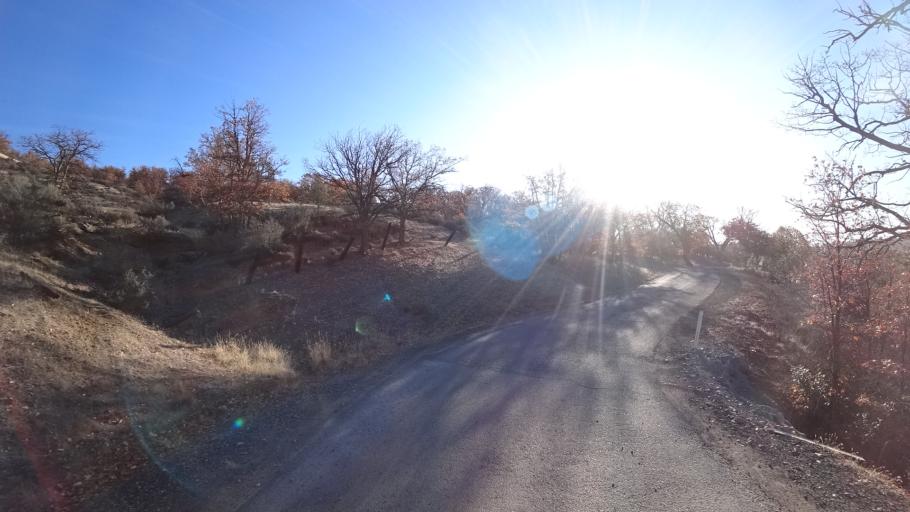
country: US
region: Oregon
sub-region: Jackson County
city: Ashland
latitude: 42.0045
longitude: -122.6434
